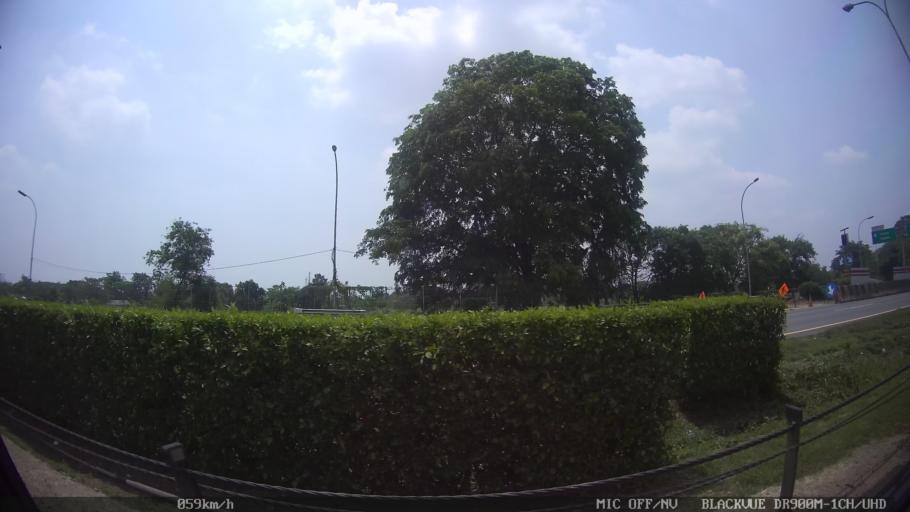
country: ID
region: West Java
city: Kresek
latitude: -6.1433
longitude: 106.2844
